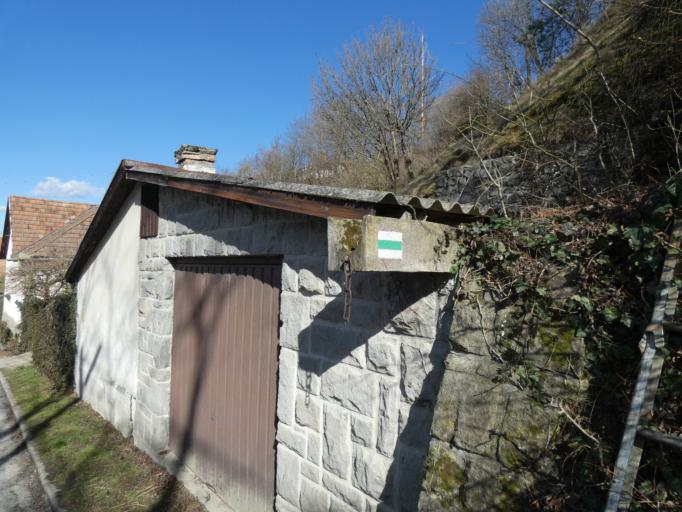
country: HU
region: Pest
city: Visegrad
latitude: 47.7786
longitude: 18.9704
